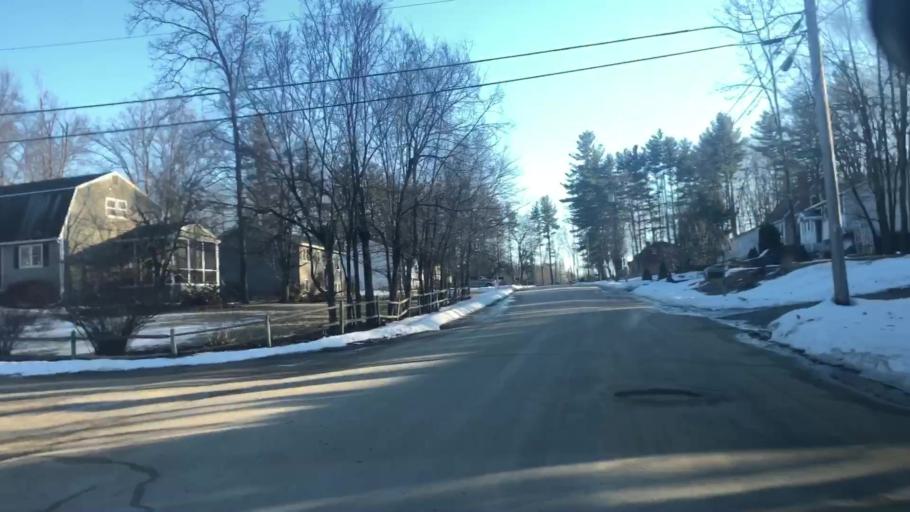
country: US
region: New Hampshire
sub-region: Hillsborough County
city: Milford
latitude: 42.8356
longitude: -71.6672
